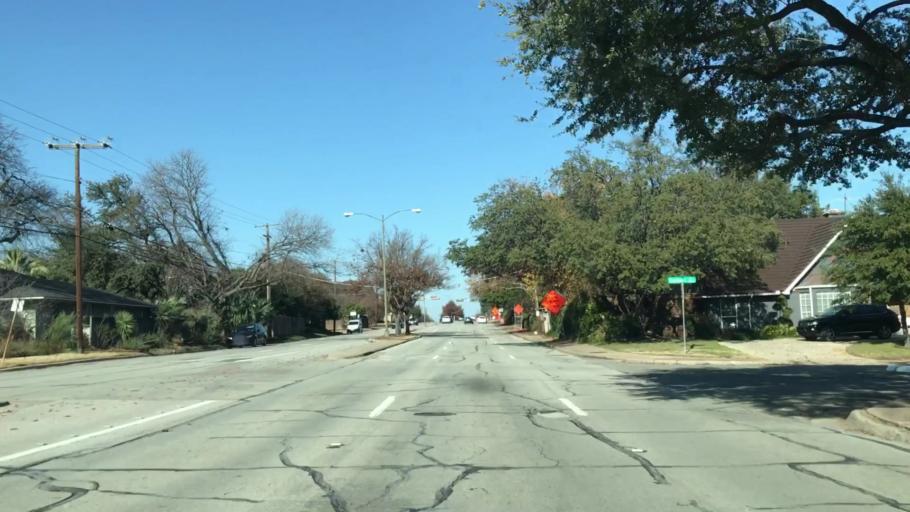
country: US
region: Texas
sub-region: Dallas County
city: University Park
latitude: 32.8779
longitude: -96.7867
